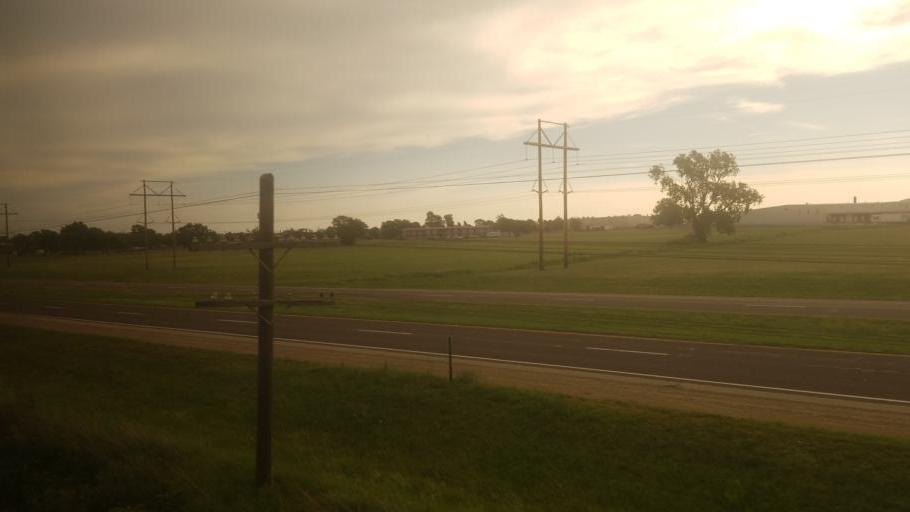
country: US
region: Kansas
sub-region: Shawnee County
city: Topeka
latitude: 38.9391
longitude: -95.6875
